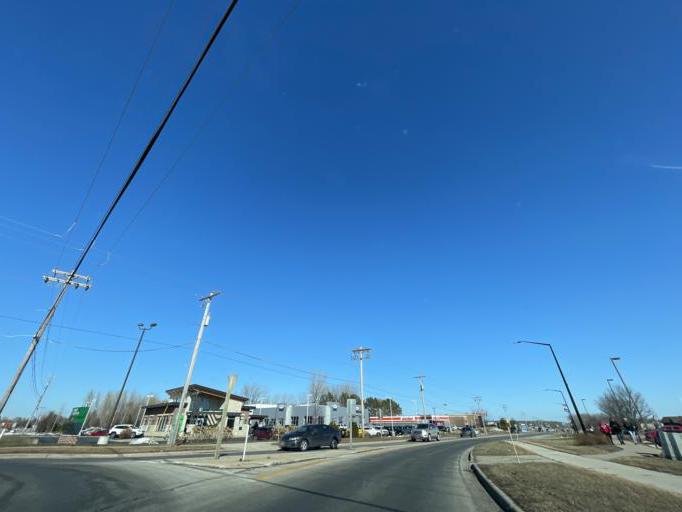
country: US
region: Wisconsin
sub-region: Brown County
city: Howard
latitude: 44.5908
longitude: -88.0842
